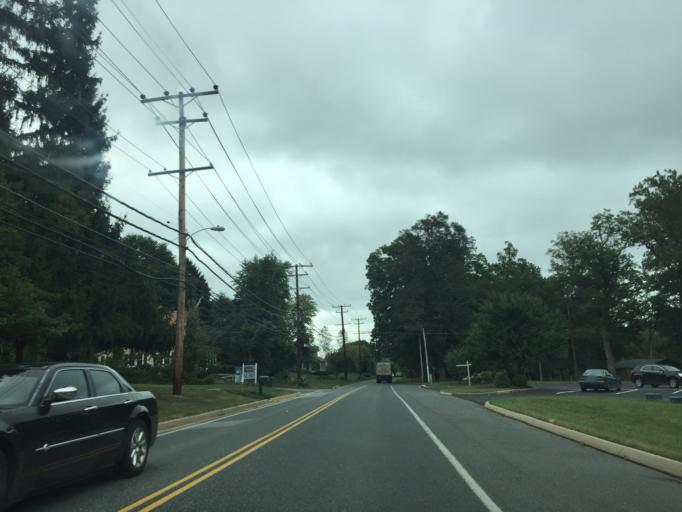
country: US
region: Maryland
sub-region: Harford County
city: Bel Air North
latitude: 39.5845
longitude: -76.3846
